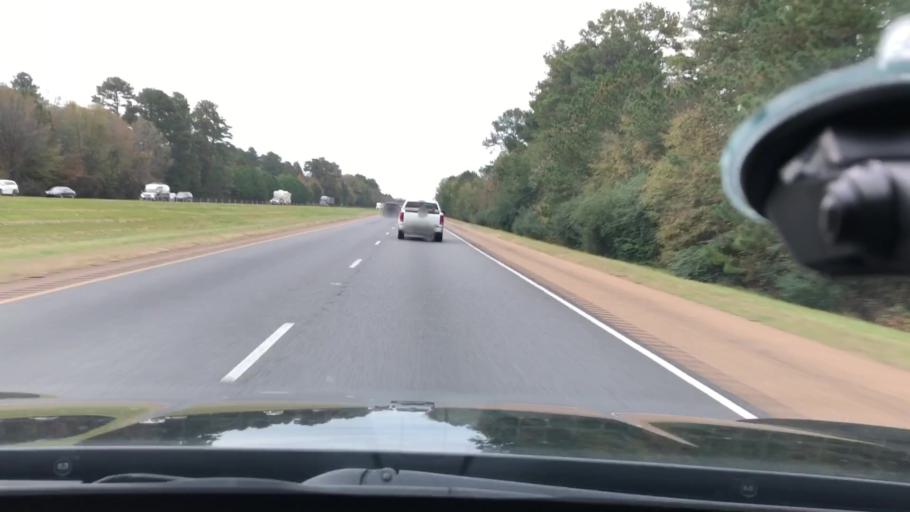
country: US
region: Arkansas
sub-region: Nevada County
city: Prescott
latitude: 33.8762
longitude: -93.3333
